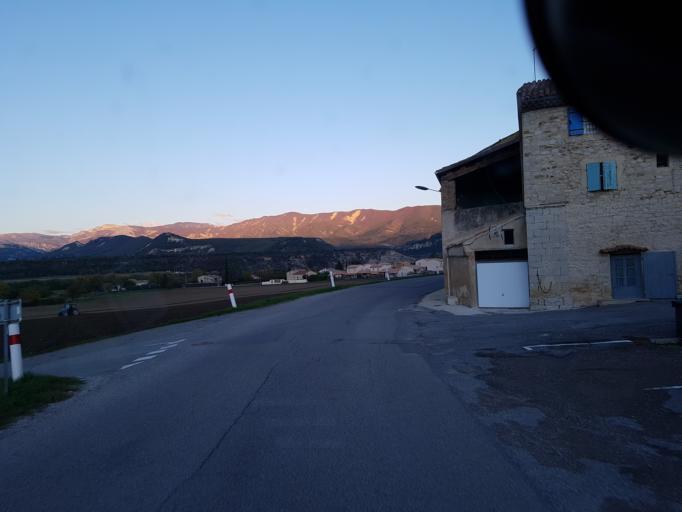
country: FR
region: Provence-Alpes-Cote d'Azur
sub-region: Departement des Alpes-de-Haute-Provence
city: Peipin
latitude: 44.1308
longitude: 5.9655
